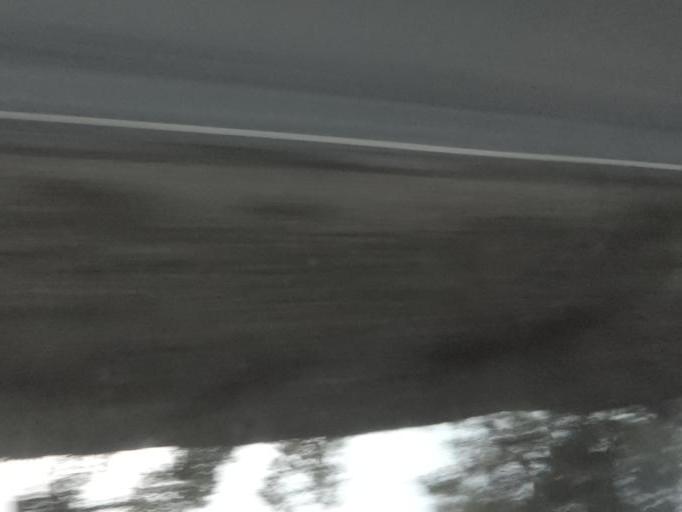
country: PT
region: Vila Real
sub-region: Sabrosa
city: Vilela
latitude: 41.2444
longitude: -7.6817
